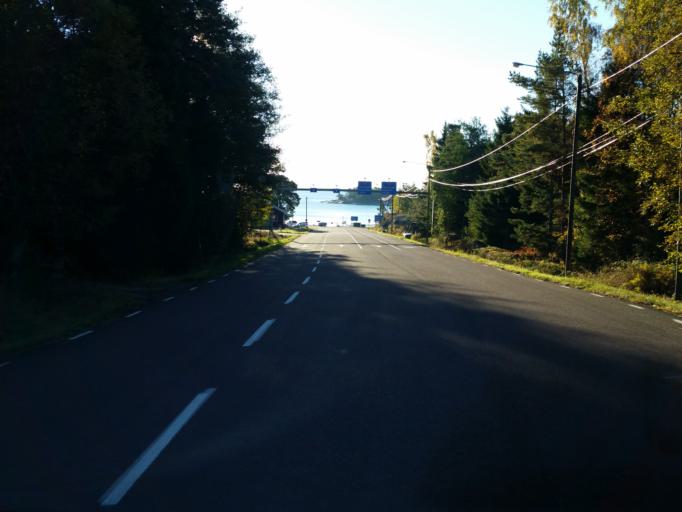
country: AX
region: Alands skaergard
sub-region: Vardoe
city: Vardoe
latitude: 60.2259
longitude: 20.4106
